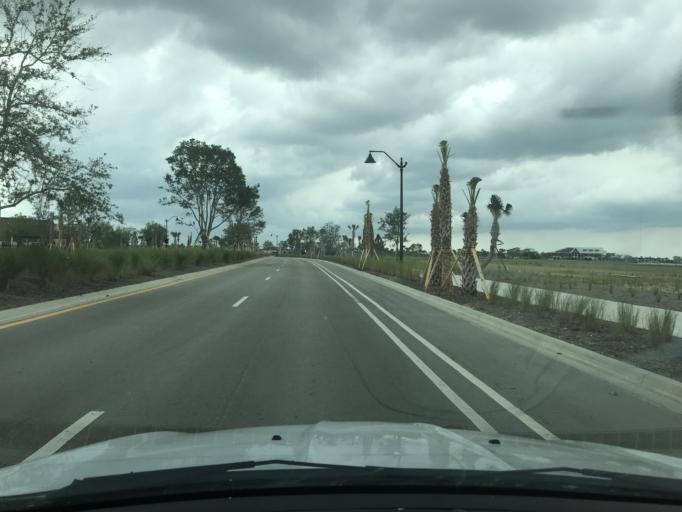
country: US
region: Florida
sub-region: Lee County
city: Olga
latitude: 26.7842
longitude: -81.7392
